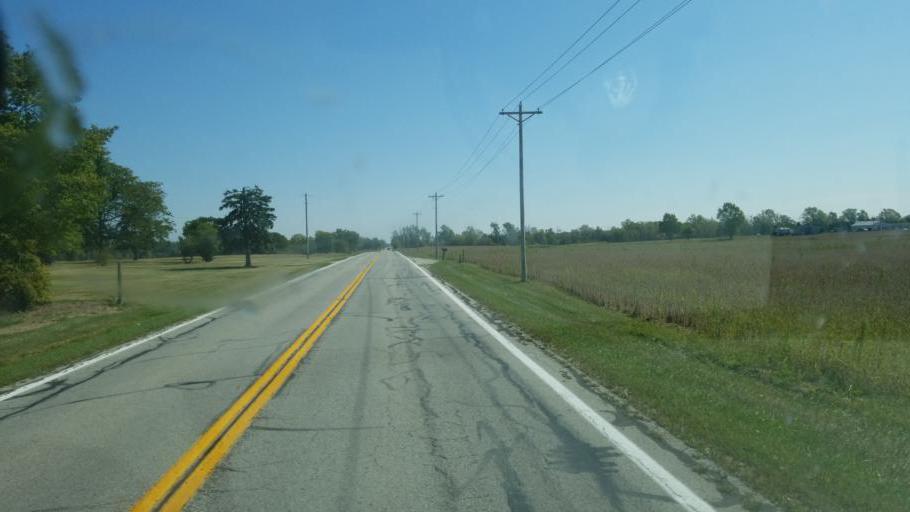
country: US
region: Ohio
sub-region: Wyandot County
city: Upper Sandusky
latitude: 40.6436
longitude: -83.3665
